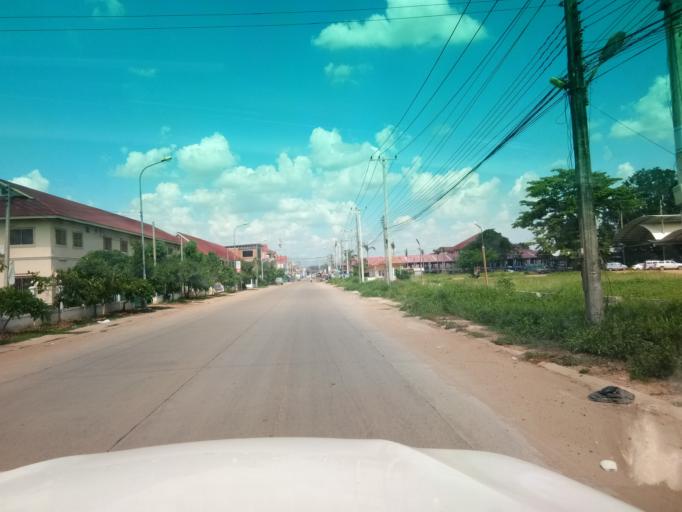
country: LA
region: Savannahkhet
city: Savannakhet
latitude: 16.5794
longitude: 104.7475
